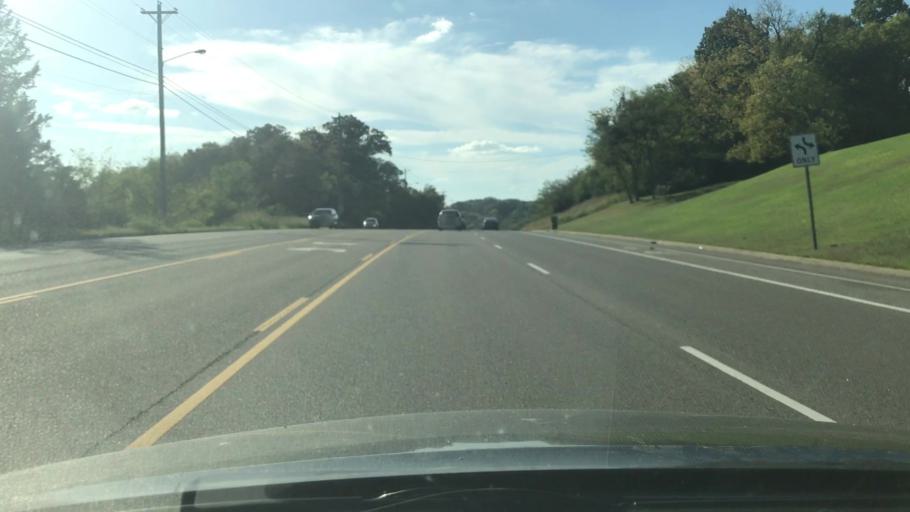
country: US
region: Tennessee
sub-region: Davidson County
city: Nashville
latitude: 36.2104
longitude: -86.8833
